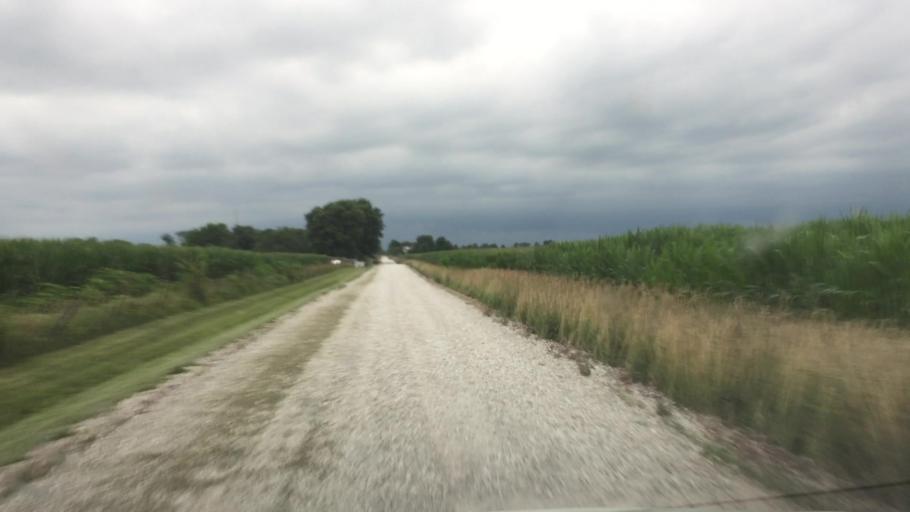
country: US
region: Illinois
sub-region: Adams County
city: Camp Point
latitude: 40.2155
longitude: -90.9608
